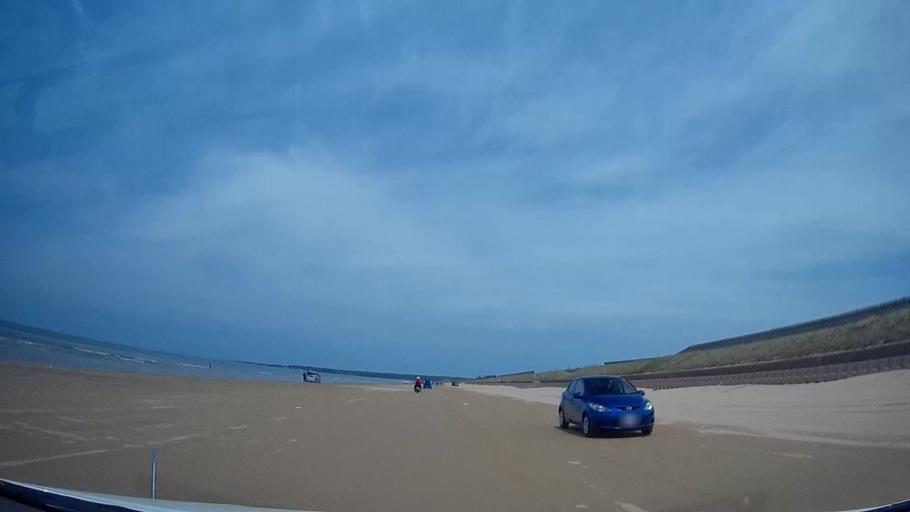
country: JP
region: Ishikawa
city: Hakui
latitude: 36.8768
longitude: 136.7615
